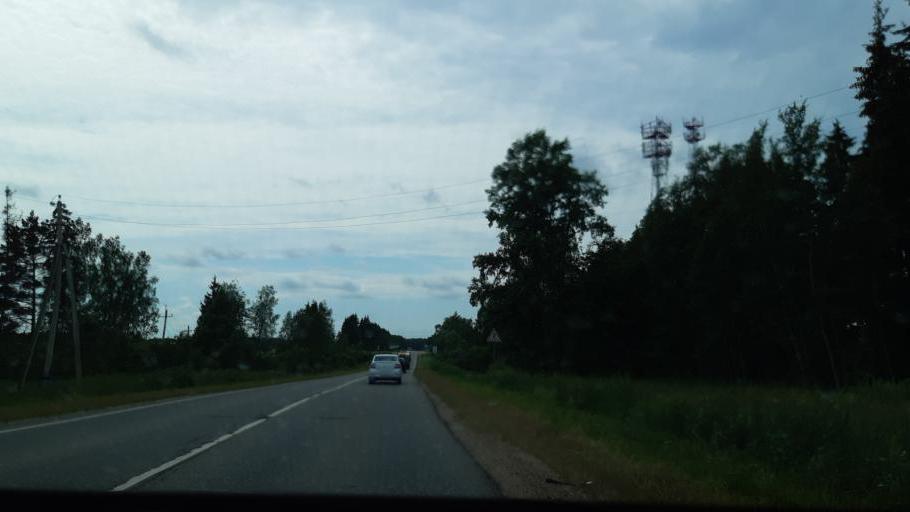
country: RU
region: Moskovskaya
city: Vereya
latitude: 55.3727
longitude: 36.2495
